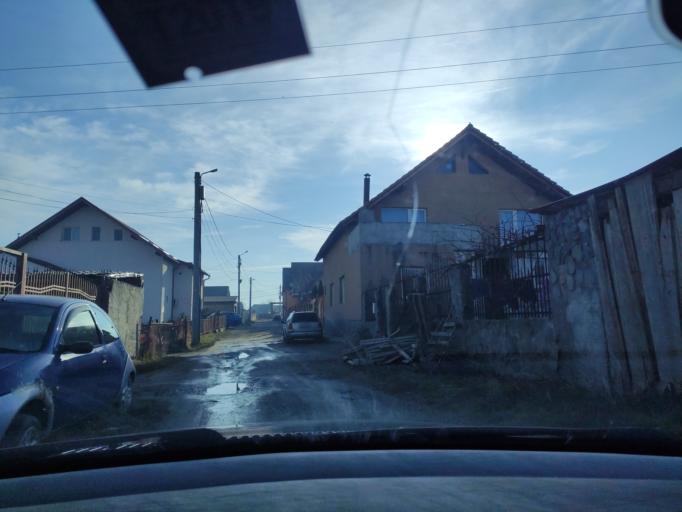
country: RO
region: Brasov
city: Codlea
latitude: 45.7060
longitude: 25.4548
